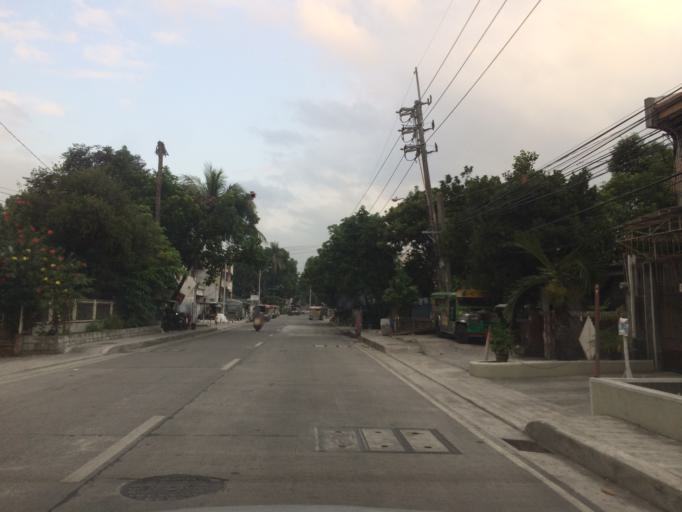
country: PH
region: Calabarzon
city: Bagong Pagasa
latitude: 14.6765
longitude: 121.0261
